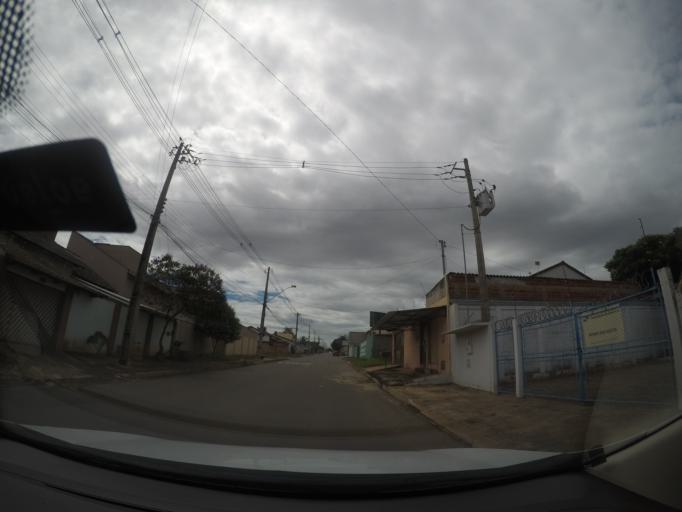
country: BR
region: Goias
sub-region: Goiania
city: Goiania
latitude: -16.7275
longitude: -49.3443
